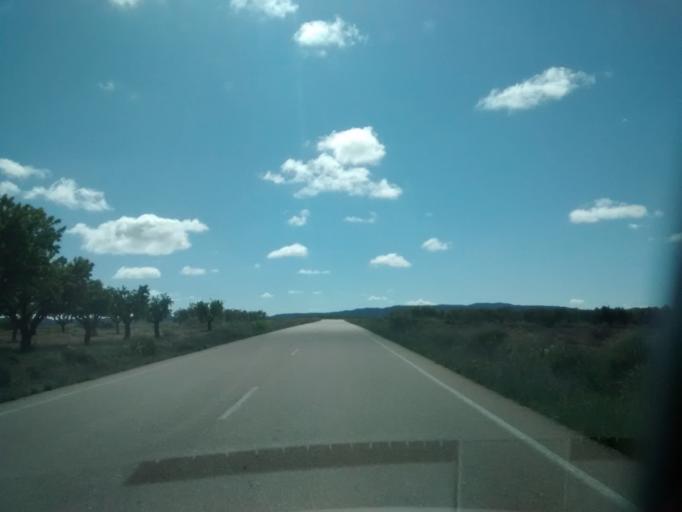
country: ES
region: Aragon
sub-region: Provincia de Zaragoza
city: Lecinena
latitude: 41.7940
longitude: -0.6429
